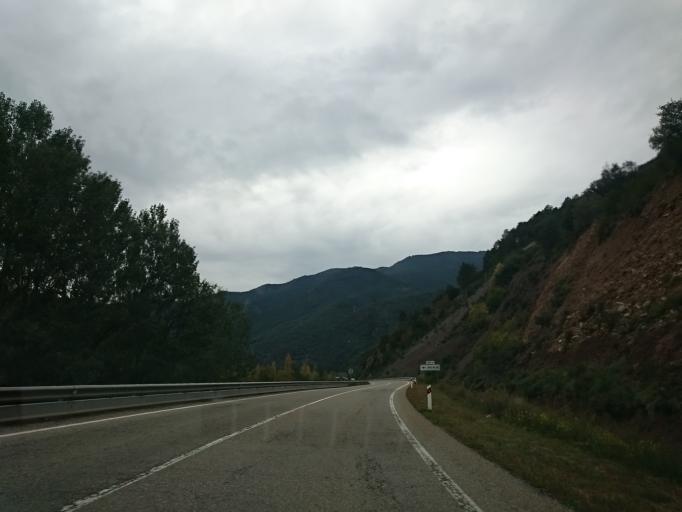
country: ES
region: Catalonia
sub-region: Provincia de Lleida
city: Sort
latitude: 42.3613
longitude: 1.0899
